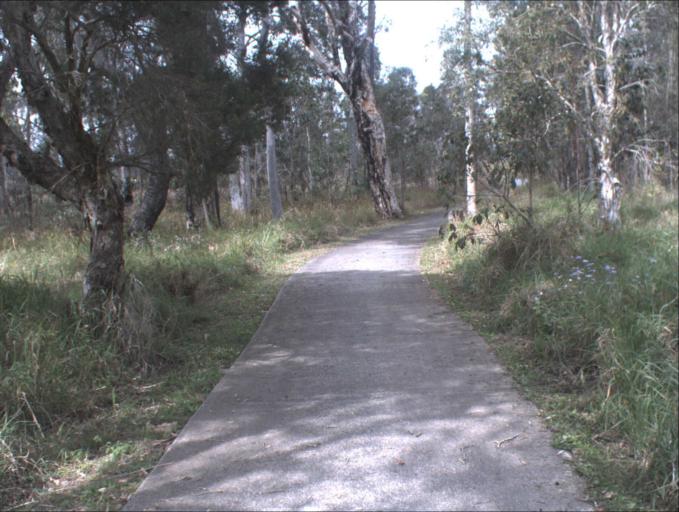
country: AU
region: Queensland
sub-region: Logan
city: Logan Reserve
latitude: -27.6868
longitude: 153.0677
